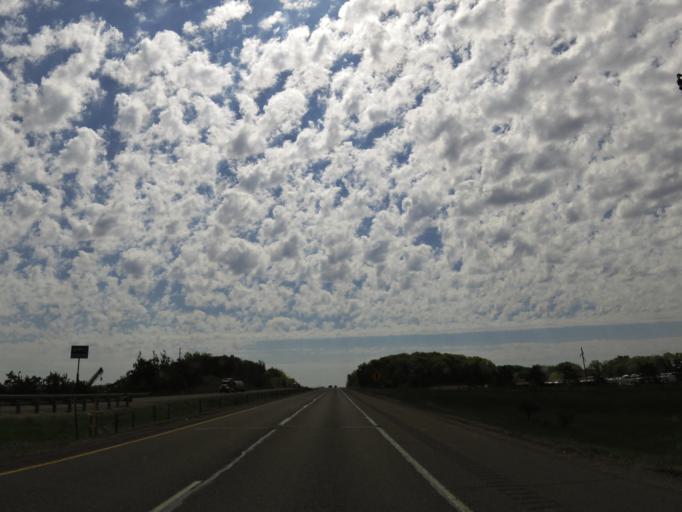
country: US
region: Wisconsin
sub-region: Dunn County
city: Colfax
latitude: 44.8853
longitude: -91.7289
